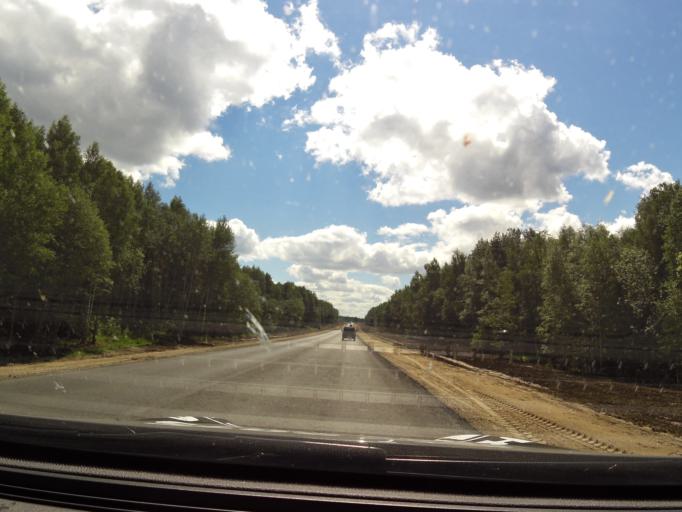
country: RU
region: Vologda
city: Molochnoye
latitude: 59.3541
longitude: 39.6761
